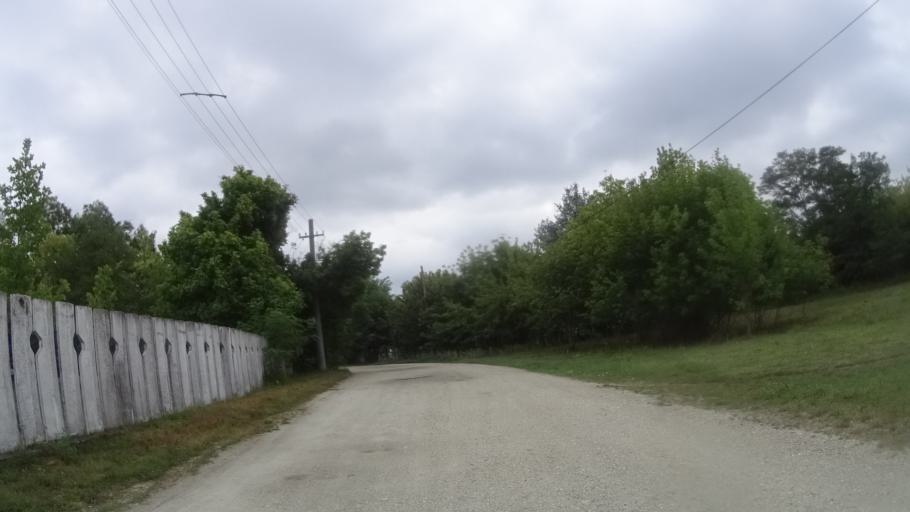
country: HU
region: Komarom-Esztergom
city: Acs
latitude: 47.7574
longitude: 17.9460
